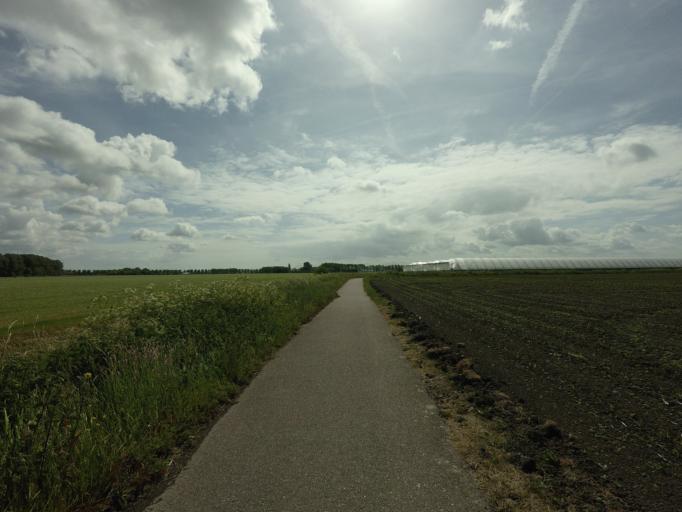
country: NL
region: North Holland
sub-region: Gemeente Opmeer
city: Opmeer
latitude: 52.6753
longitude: 5.0017
